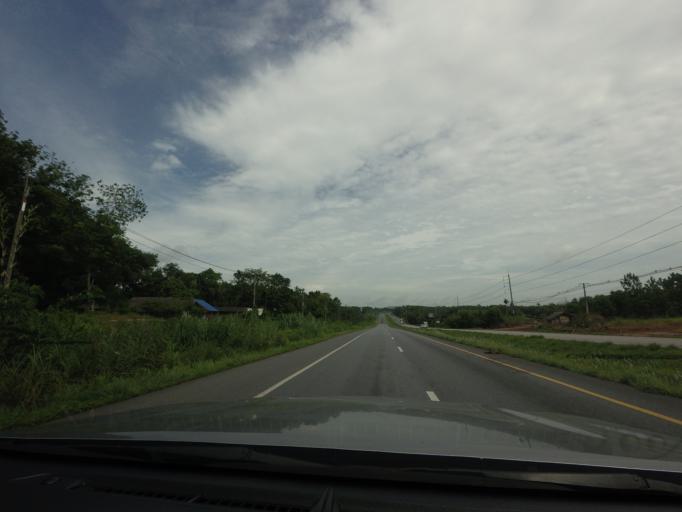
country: TH
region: Nakhon Si Thammarat
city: Thung Yai
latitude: 8.3293
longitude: 99.4423
